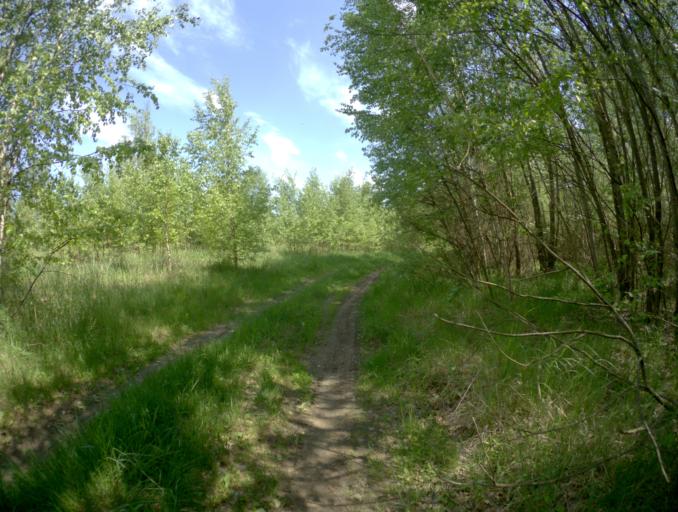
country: RU
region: Vladimir
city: Gusevskiy
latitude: 55.6727
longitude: 40.4699
